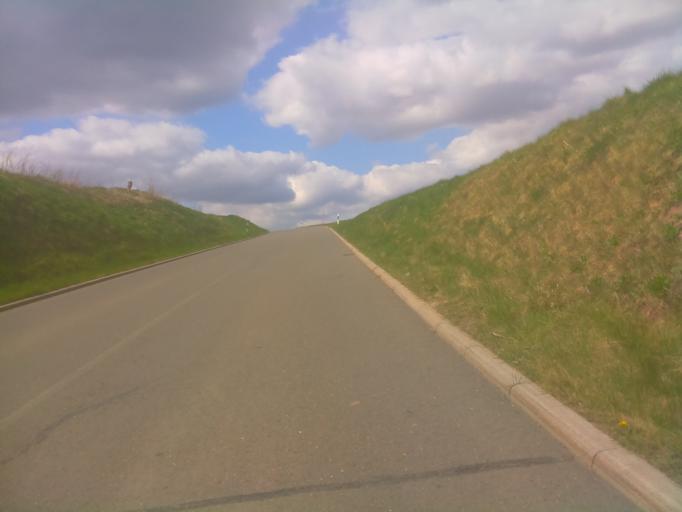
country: DE
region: Thuringia
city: Gneus
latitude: 50.8347
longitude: 11.6847
